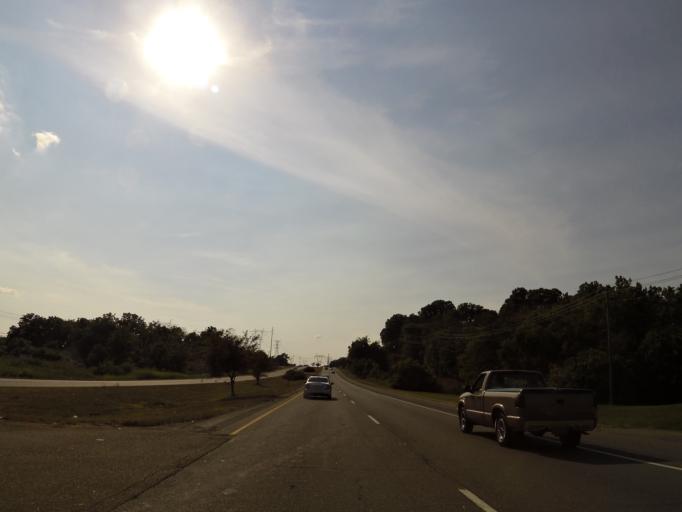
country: US
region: Tennessee
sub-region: Blount County
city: Maryville
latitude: 35.7526
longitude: -84.0053
